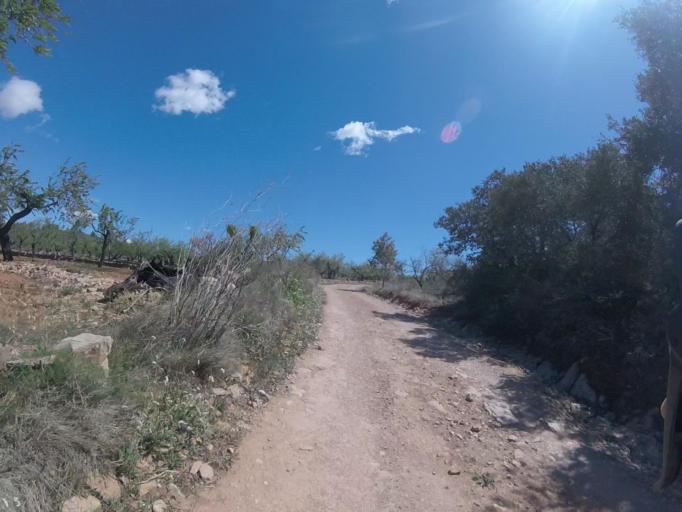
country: ES
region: Valencia
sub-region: Provincia de Castello
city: Cabanes
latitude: 40.1554
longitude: 0.0939
